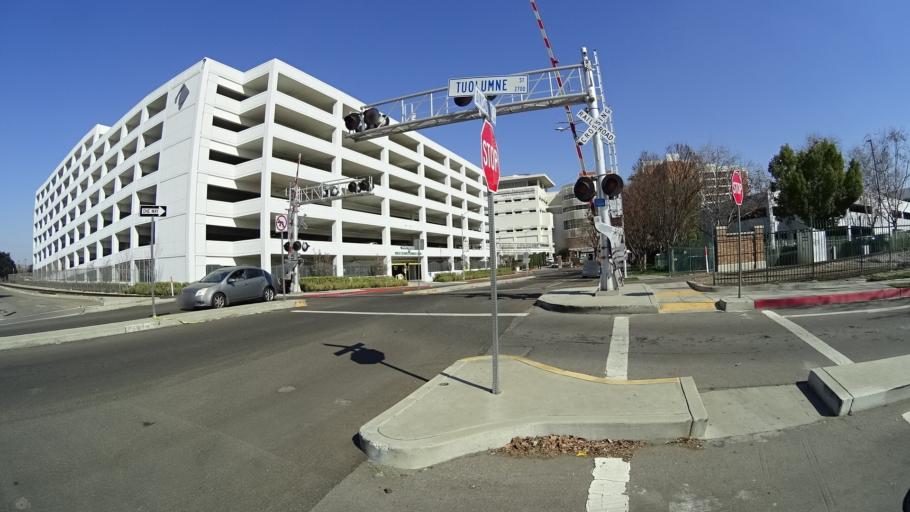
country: US
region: California
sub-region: Fresno County
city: Fresno
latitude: 36.7434
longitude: -119.7864
